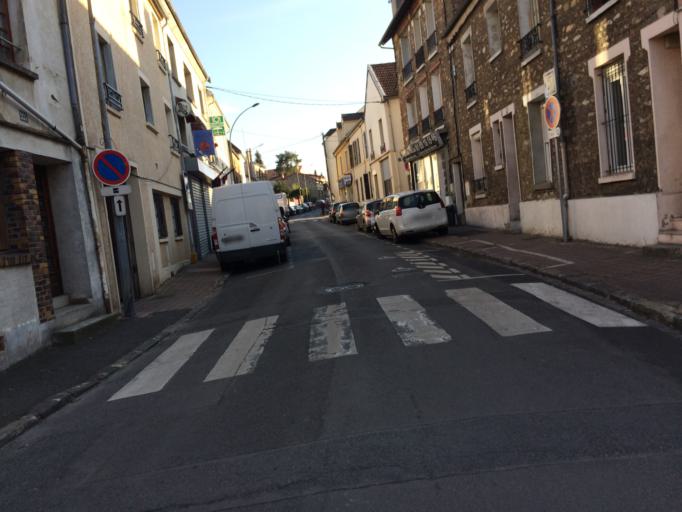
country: FR
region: Ile-de-France
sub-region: Departement de l'Essonne
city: Villebon-sur-Yvette
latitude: 48.7094
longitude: 2.2408
